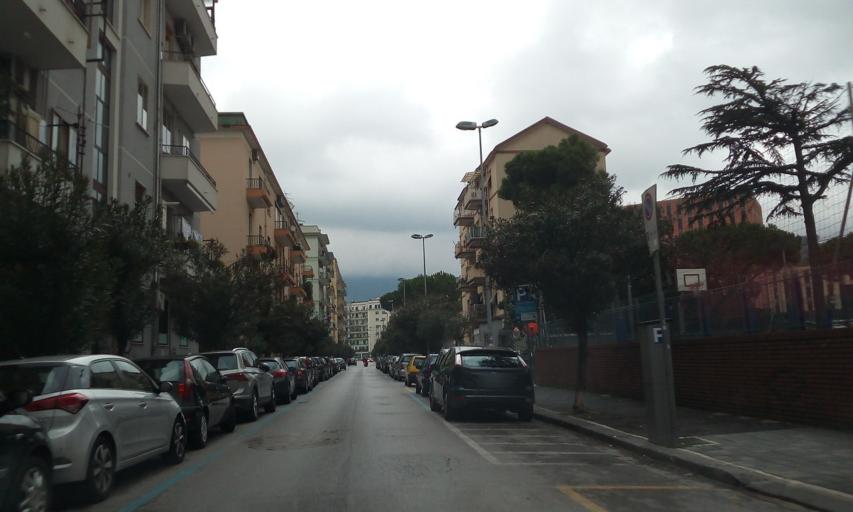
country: IT
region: Campania
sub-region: Provincia di Salerno
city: Salerno
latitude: 40.6785
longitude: 14.7716
